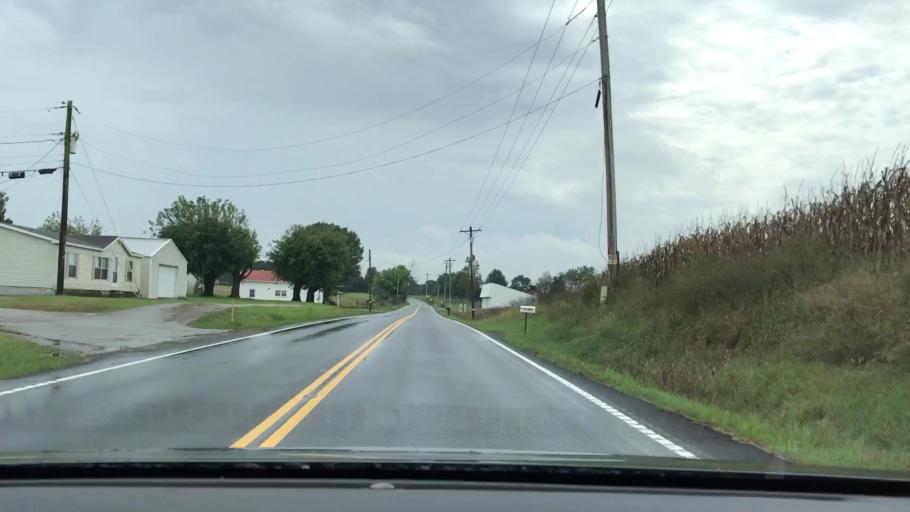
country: US
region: Tennessee
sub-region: Macon County
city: Red Boiling Springs
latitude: 36.5046
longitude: -85.8654
